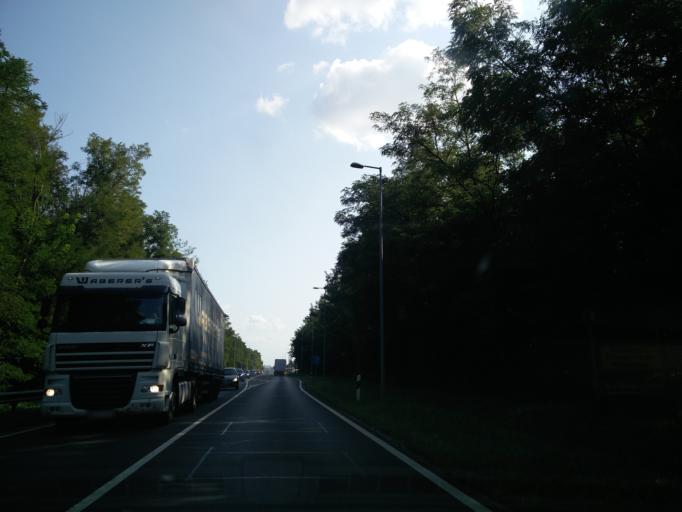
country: HU
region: Zala
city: Zalaegerszeg
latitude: 46.8692
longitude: 16.8535
